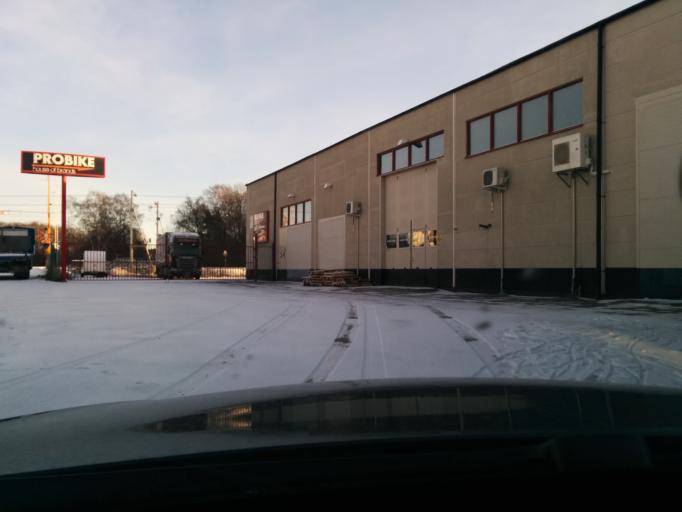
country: SE
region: Stockholm
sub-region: Taby Kommun
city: Taby
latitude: 59.4836
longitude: 18.0583
